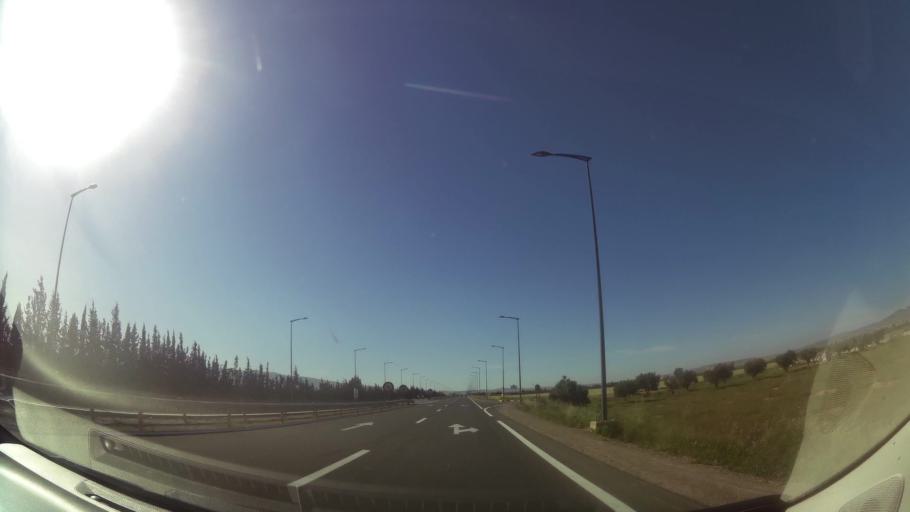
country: MA
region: Oriental
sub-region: Oujda-Angad
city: Oujda
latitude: 34.8155
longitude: -1.9644
